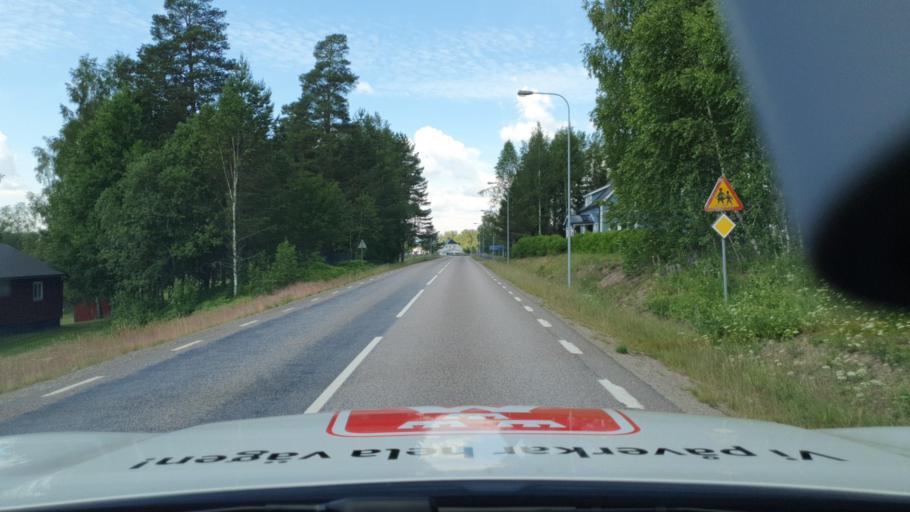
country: SE
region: Vaermland
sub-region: Torsby Kommun
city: Torsby
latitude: 60.3408
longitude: 12.9875
